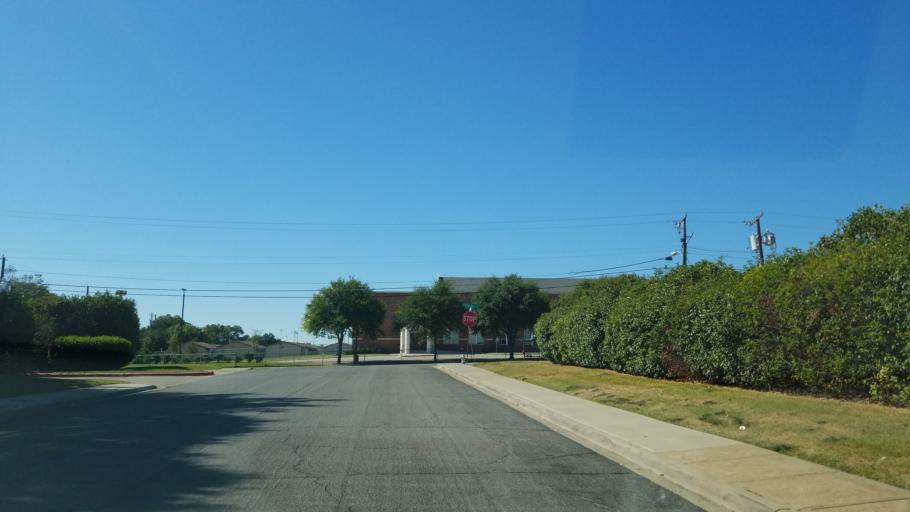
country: US
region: Texas
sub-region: Dallas County
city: Highland Park
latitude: 32.8069
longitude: -96.7480
